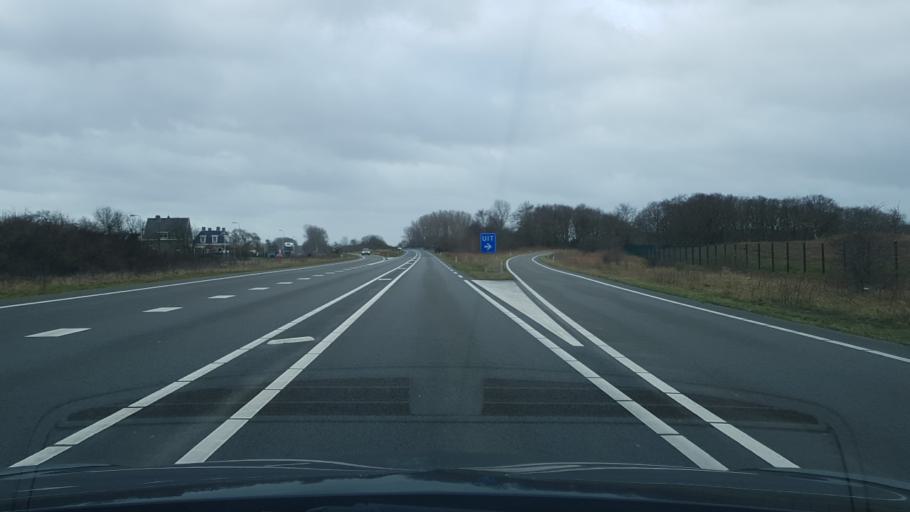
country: NL
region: South Holland
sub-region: Gemeente Lisse
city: Lisse
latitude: 52.2954
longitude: 4.5290
